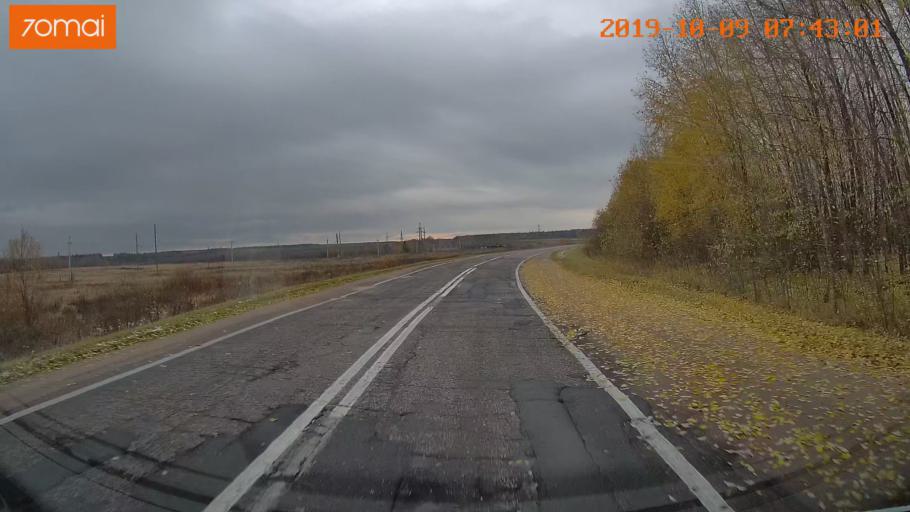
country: RU
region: Jaroslavl
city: Kukoboy
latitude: 58.6449
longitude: 39.7291
